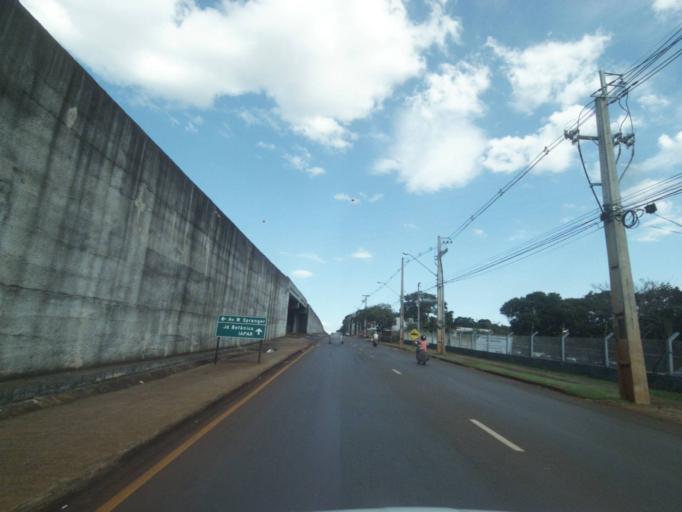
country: BR
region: Parana
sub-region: Londrina
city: Londrina
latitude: -23.3471
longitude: -51.1730
